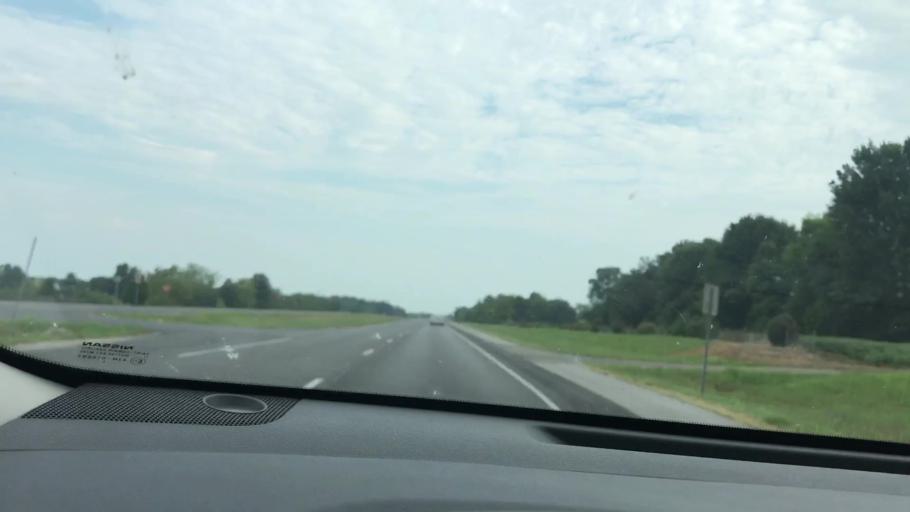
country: US
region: Kentucky
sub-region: Calloway County
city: Murray
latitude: 36.6913
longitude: -88.3030
